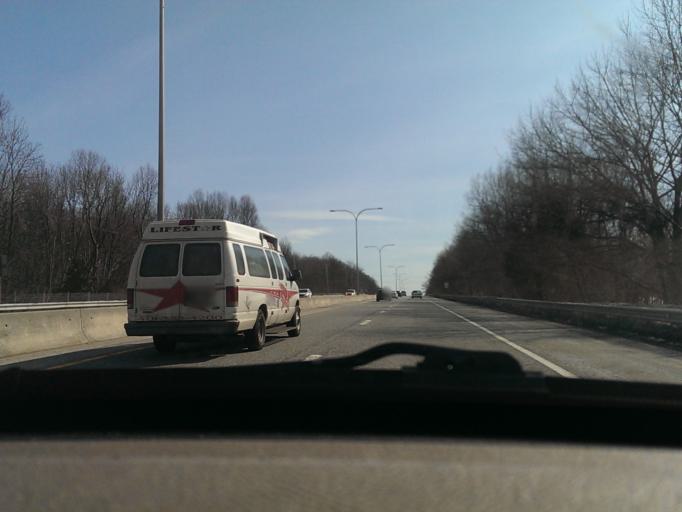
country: US
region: Rhode Island
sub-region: Providence County
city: Central Falls
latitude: 41.8868
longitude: -71.4382
